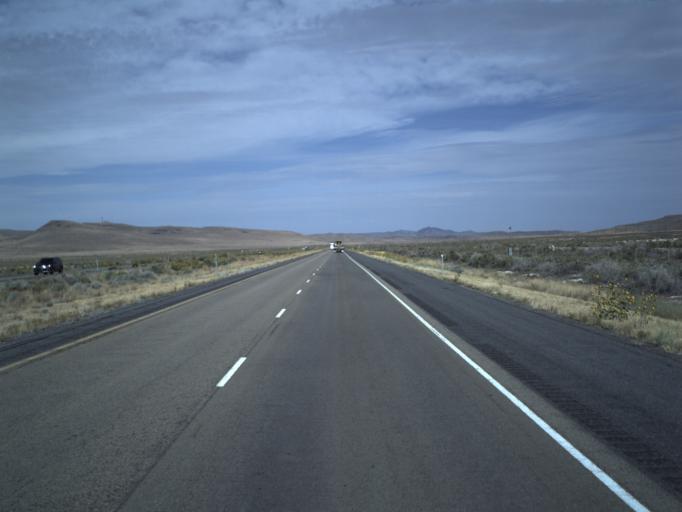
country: US
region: Utah
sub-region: Tooele County
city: Grantsville
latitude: 40.7737
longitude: -112.8009
